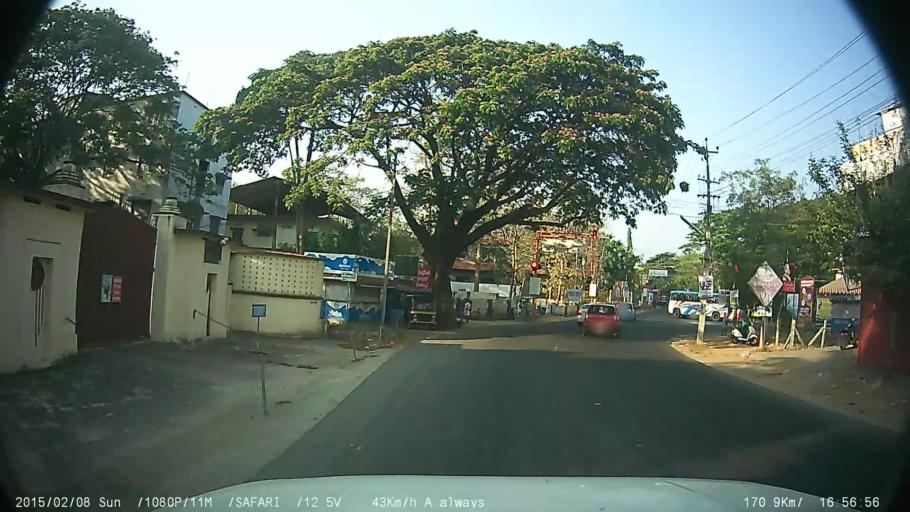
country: IN
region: Kerala
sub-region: Palakkad district
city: Palakkad
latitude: 10.7610
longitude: 76.6545
